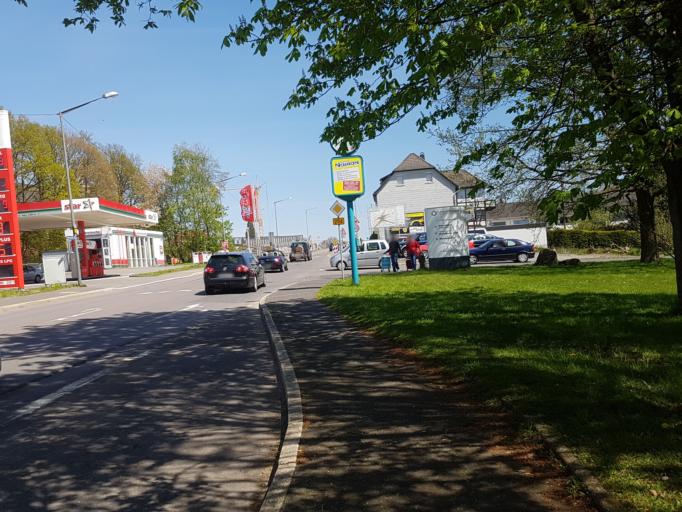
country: DE
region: North Rhine-Westphalia
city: Waldbrol
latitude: 50.8816
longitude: 7.6290
